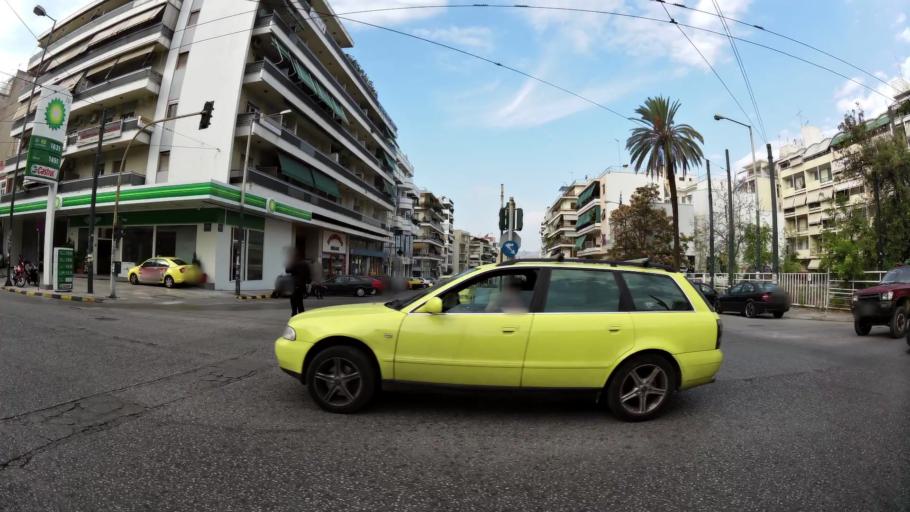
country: GR
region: Attica
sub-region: Nomarchia Athinas
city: Nea Chalkidona
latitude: 38.0196
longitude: 23.7355
